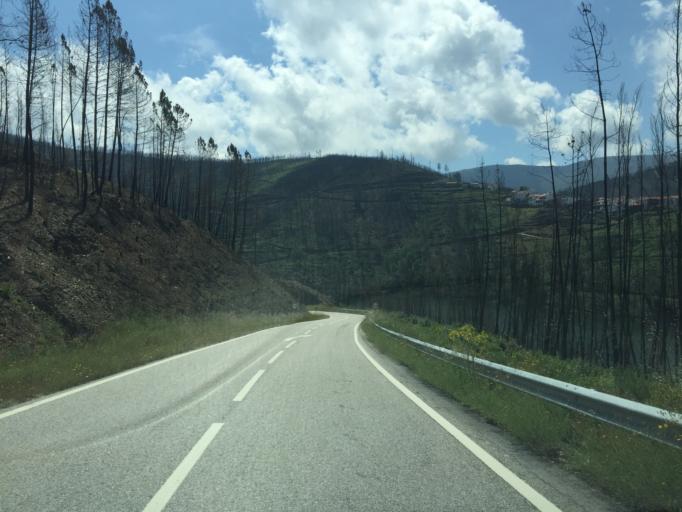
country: PT
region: Coimbra
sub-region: Pampilhosa da Serra
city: Pampilhosa da Serra
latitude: 39.9803
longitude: -7.9663
